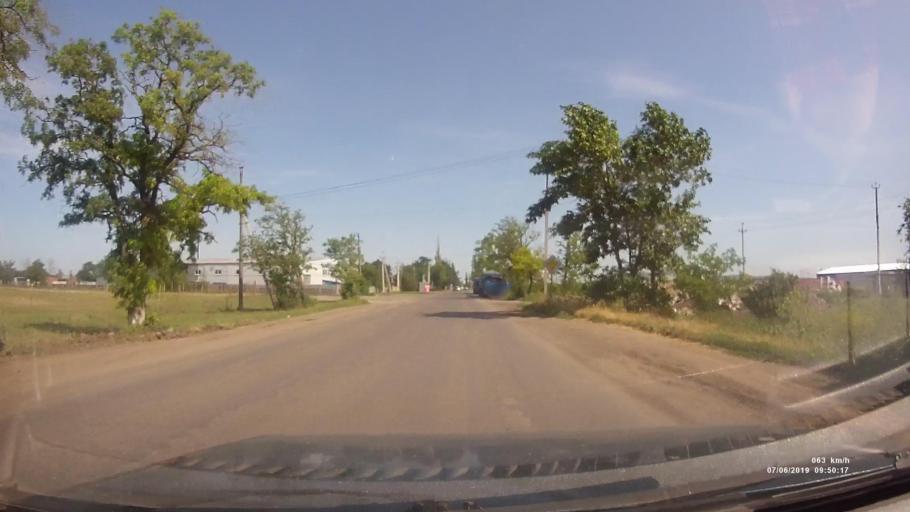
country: RU
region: Rostov
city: Azov
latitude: 47.0782
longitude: 39.4375
